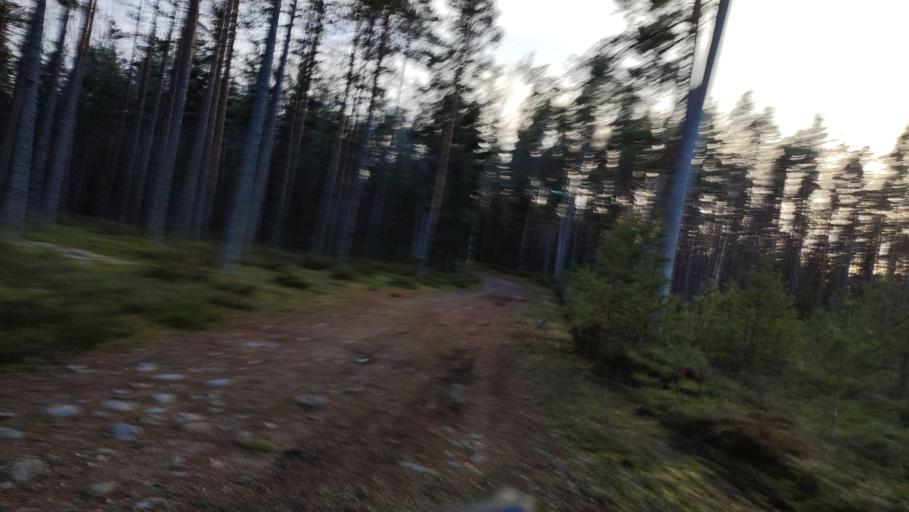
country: FI
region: Southern Ostrobothnia
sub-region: Suupohja
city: Karijoki
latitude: 62.2770
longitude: 21.6287
